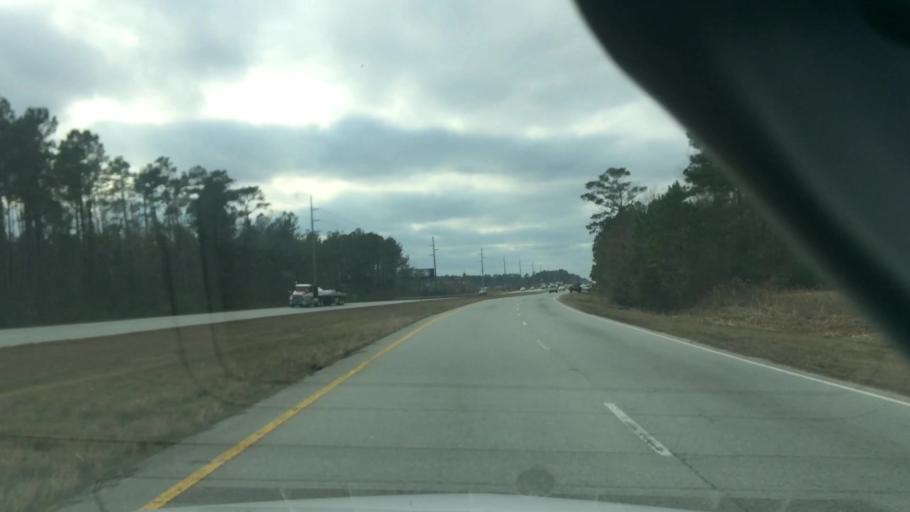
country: US
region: North Carolina
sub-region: Brunswick County
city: Shallotte
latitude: 33.9588
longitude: -78.4223
